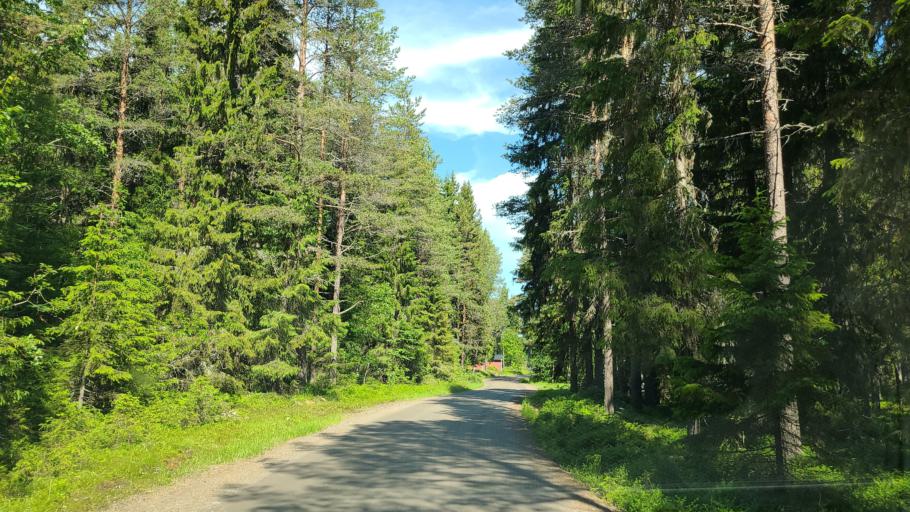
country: SE
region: Vaesterbotten
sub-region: Robertsfors Kommun
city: Robertsfors
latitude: 64.1421
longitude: 20.9605
